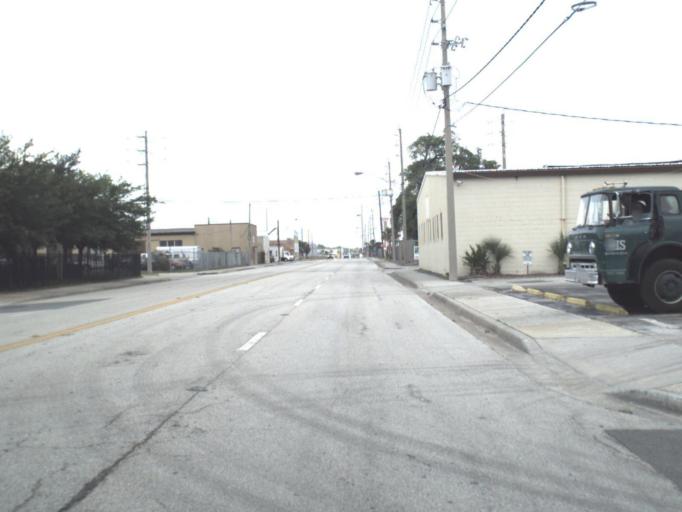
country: US
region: Florida
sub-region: Duval County
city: Jacksonville
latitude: 30.3288
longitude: -81.6317
